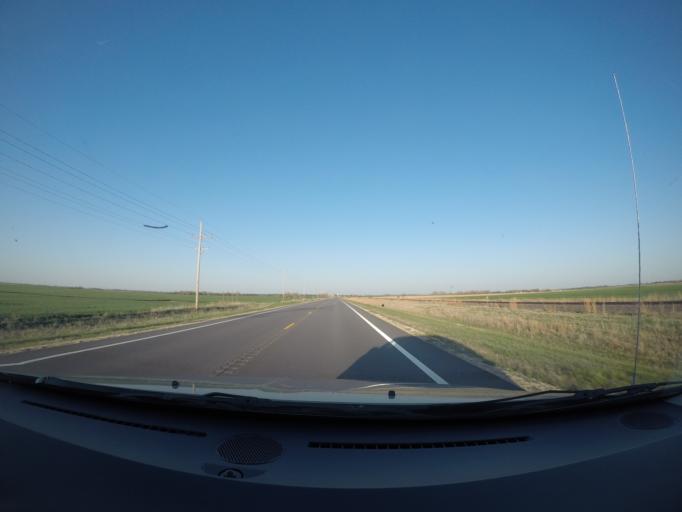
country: US
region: Kansas
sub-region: Stafford County
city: Stafford
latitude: 37.8227
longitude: -98.4007
